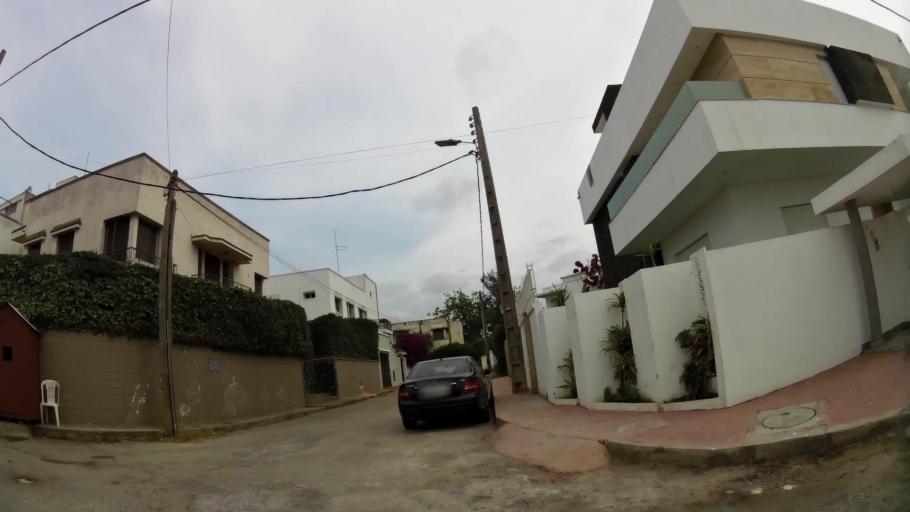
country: MA
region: Rabat-Sale-Zemmour-Zaer
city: Sale
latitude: 34.0320
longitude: -6.8138
